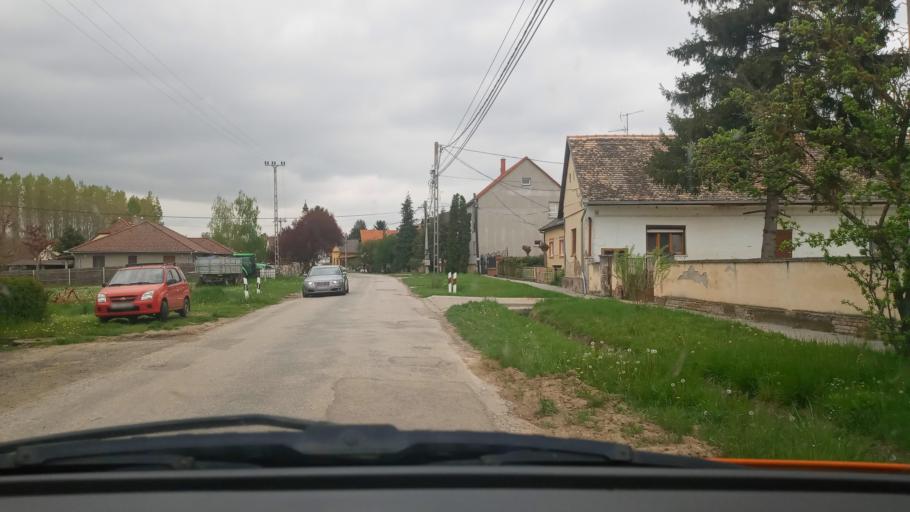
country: HU
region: Baranya
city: Boly
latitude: 46.0028
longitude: 18.5532
